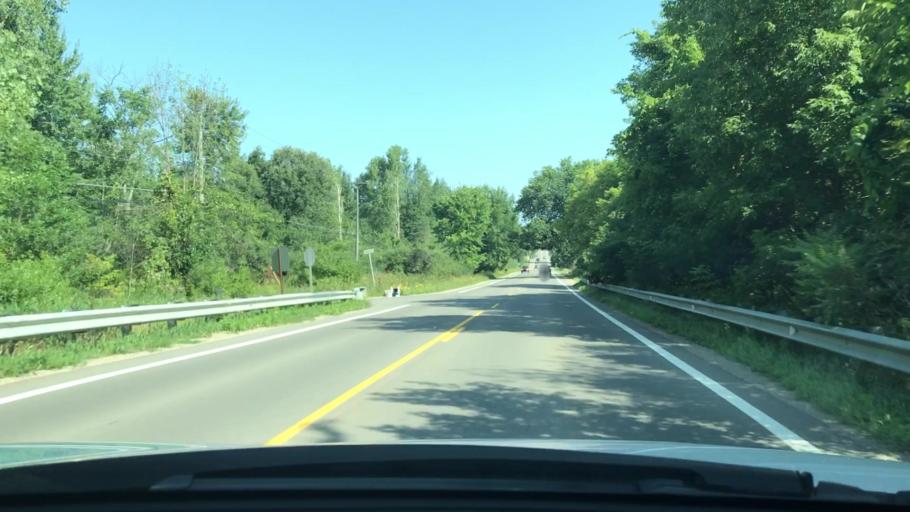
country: US
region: Michigan
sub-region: Oakland County
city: Oxford
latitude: 42.8021
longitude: -83.3333
